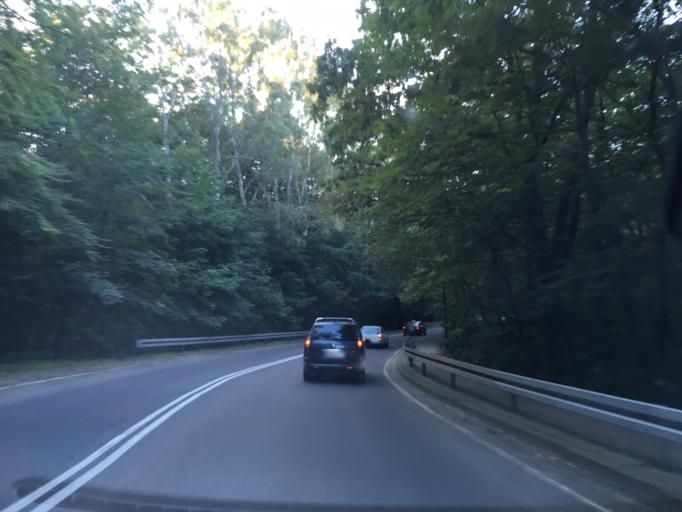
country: PL
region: Pomeranian Voivodeship
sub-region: Sopot
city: Sopot
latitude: 54.4548
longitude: 18.5384
